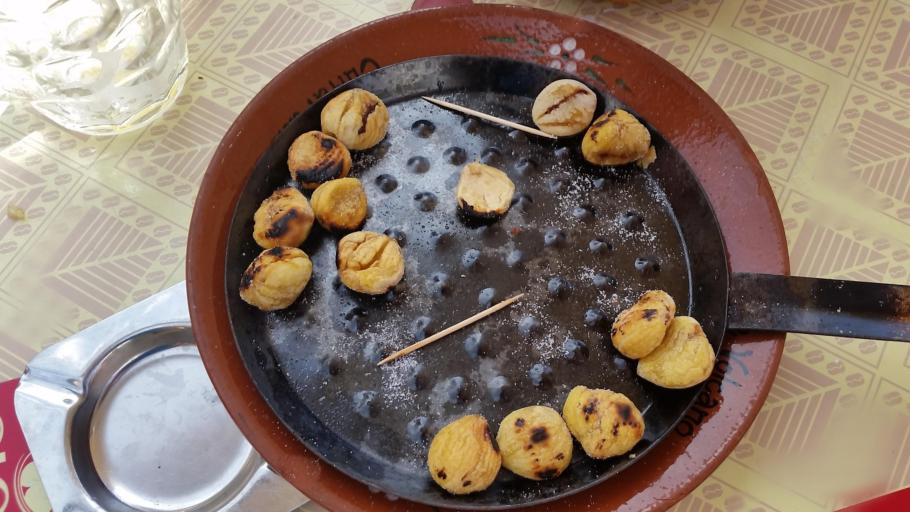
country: PT
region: Madeira
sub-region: Camara de Lobos
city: Curral das Freiras
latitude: 32.7204
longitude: -16.9651
